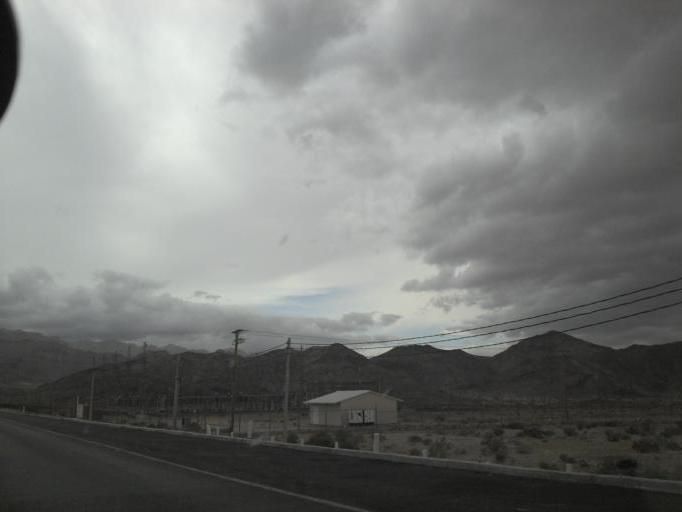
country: MX
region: Baja California
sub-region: Tecate
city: Cereso del Hongo
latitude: 32.5671
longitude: -115.9374
